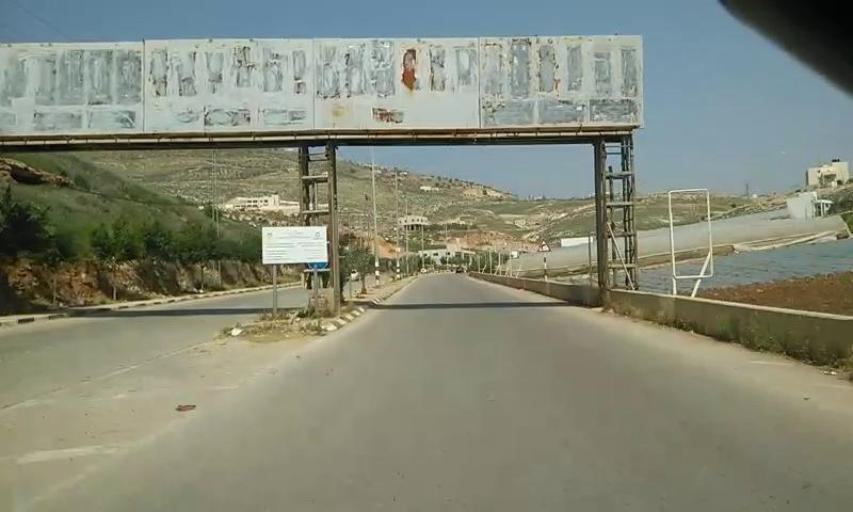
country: PS
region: West Bank
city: Tubas
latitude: 32.3052
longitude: 35.3638
